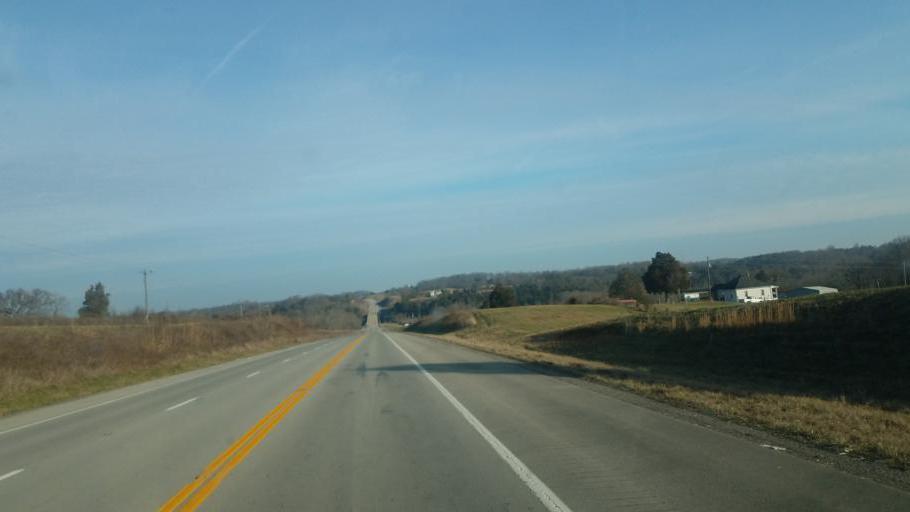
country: US
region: Kentucky
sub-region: Russell County
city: Jamestown
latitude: 36.9605
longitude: -85.0893
